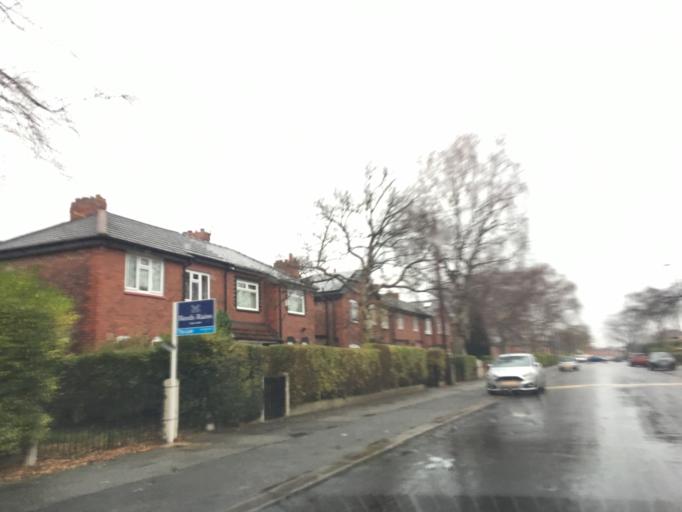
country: GB
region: England
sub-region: Manchester
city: Chorlton cum Hardy
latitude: 53.4259
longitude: -2.2646
